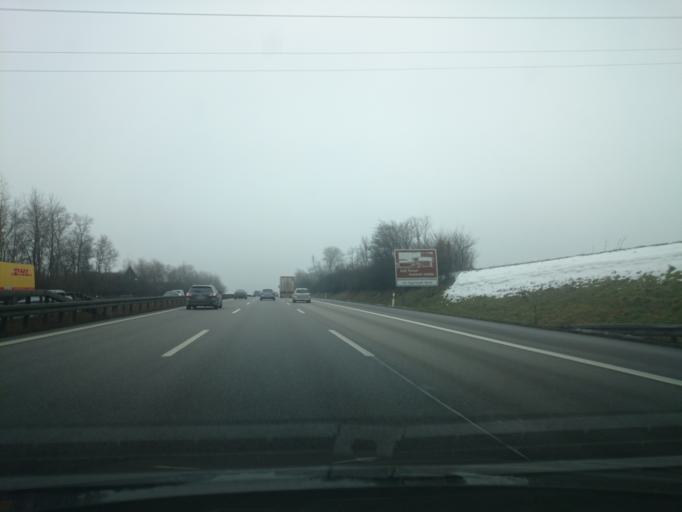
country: DE
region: Bavaria
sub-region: Upper Bavaria
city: Lenting
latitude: 48.8008
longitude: 11.4645
